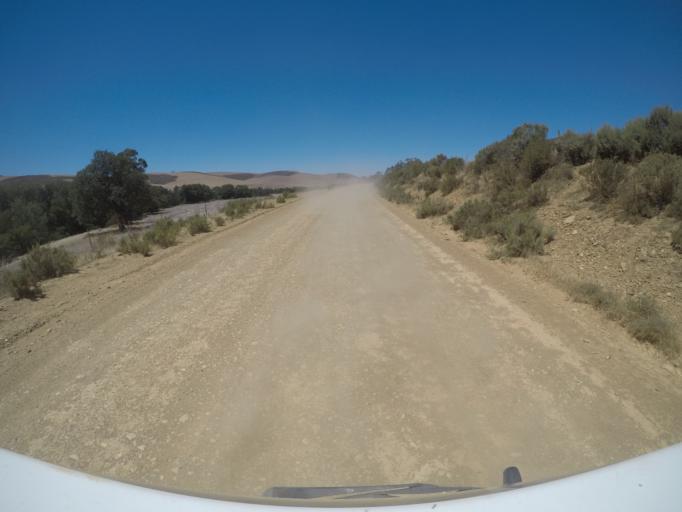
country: ZA
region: Western Cape
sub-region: Overberg District Municipality
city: Grabouw
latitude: -34.0965
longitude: 19.1985
